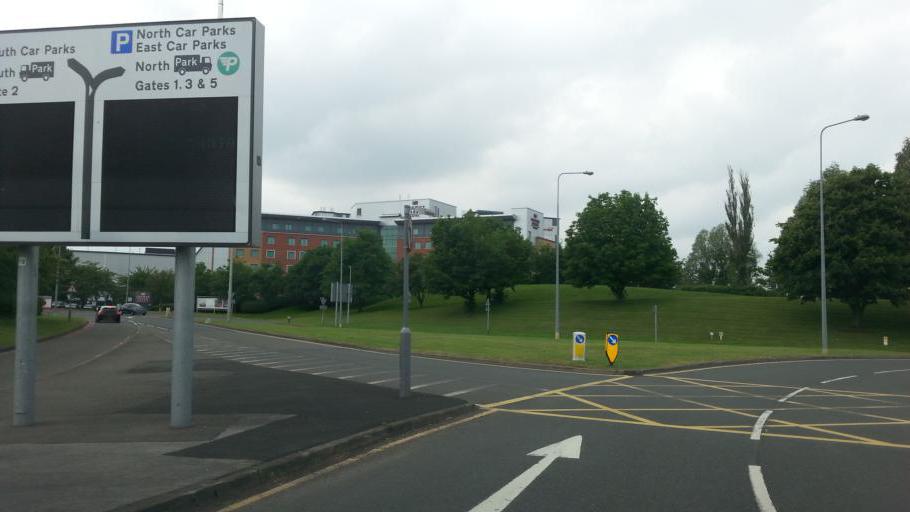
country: GB
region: England
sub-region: Solihull
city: Bickenhill
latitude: 52.4474
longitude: -1.7134
